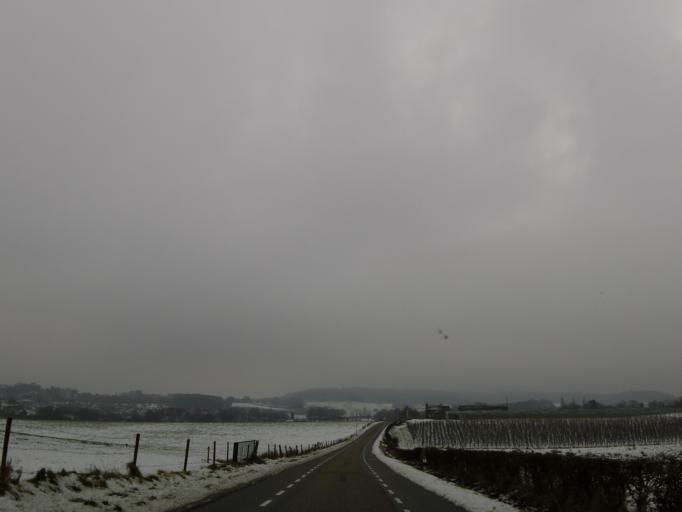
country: NL
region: Limburg
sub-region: Gemeente Vaals
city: Vaals
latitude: 50.7717
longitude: 5.9887
